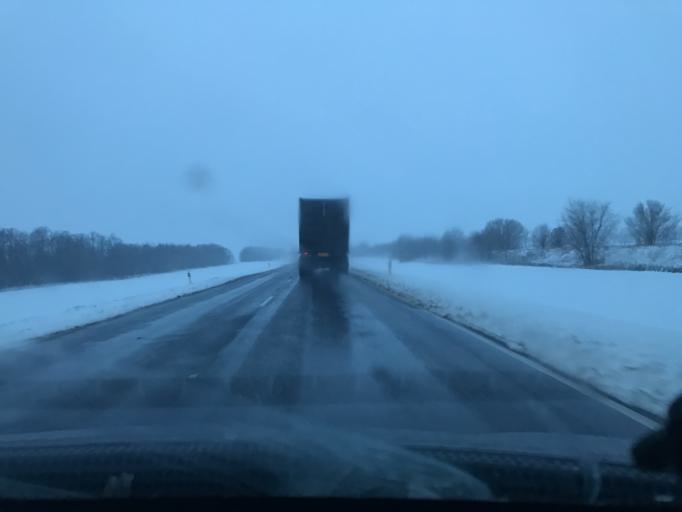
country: RU
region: Rostov
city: Letnik
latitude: 46.0381
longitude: 41.2110
